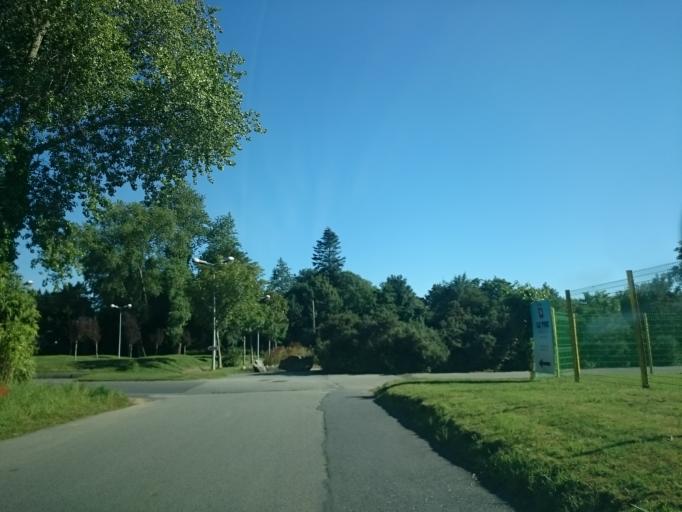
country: FR
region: Brittany
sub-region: Departement du Finistere
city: Brest
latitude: 48.4249
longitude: -4.4701
